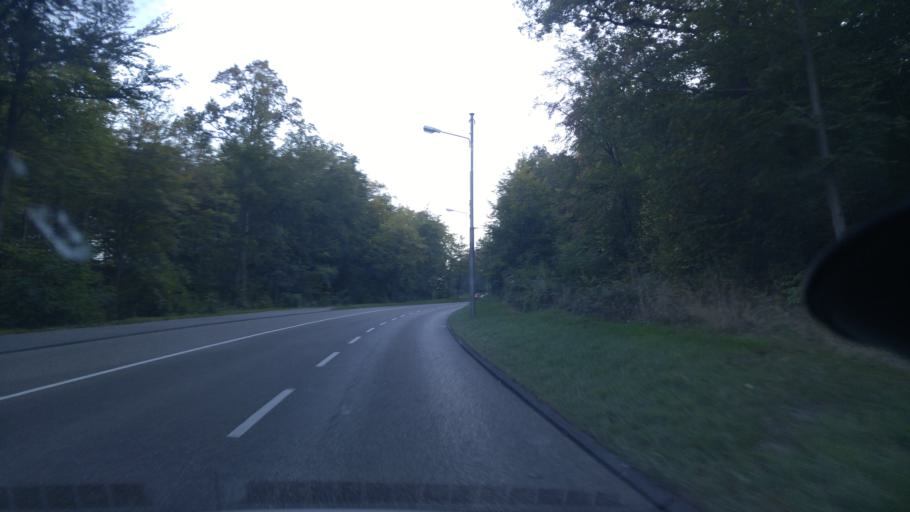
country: DE
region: Baden-Wuerttemberg
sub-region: Regierungsbezirk Stuttgart
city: Stuttgart
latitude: 48.7684
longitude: 9.1344
